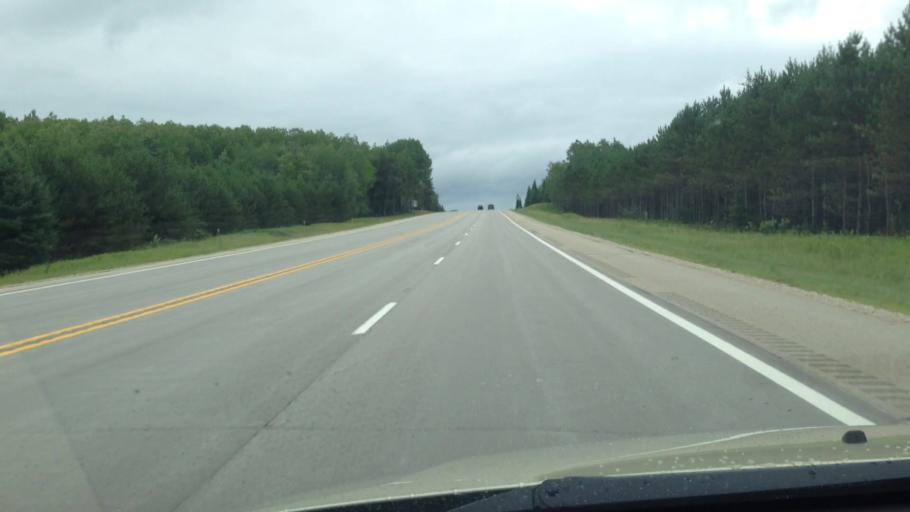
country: US
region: Michigan
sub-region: Schoolcraft County
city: Manistique
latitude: 45.9089
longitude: -86.4383
